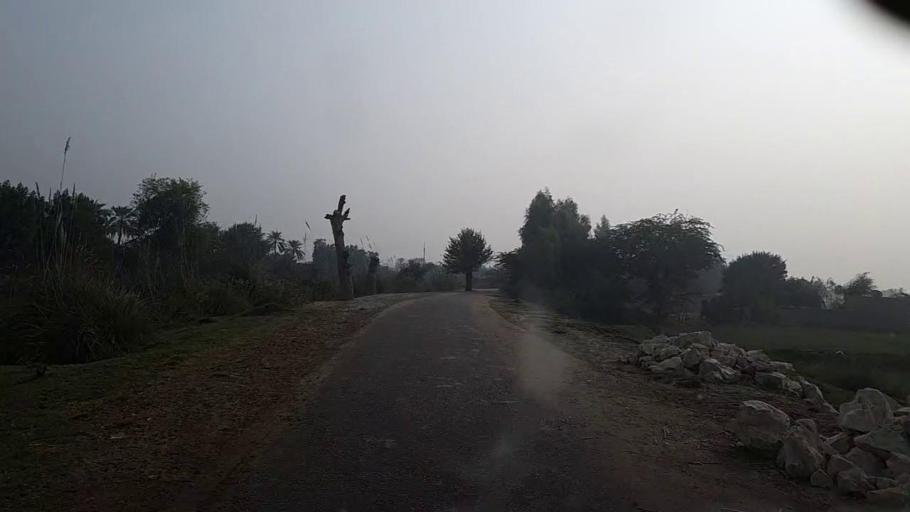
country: PK
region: Sindh
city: Bozdar
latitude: 27.1361
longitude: 68.6536
